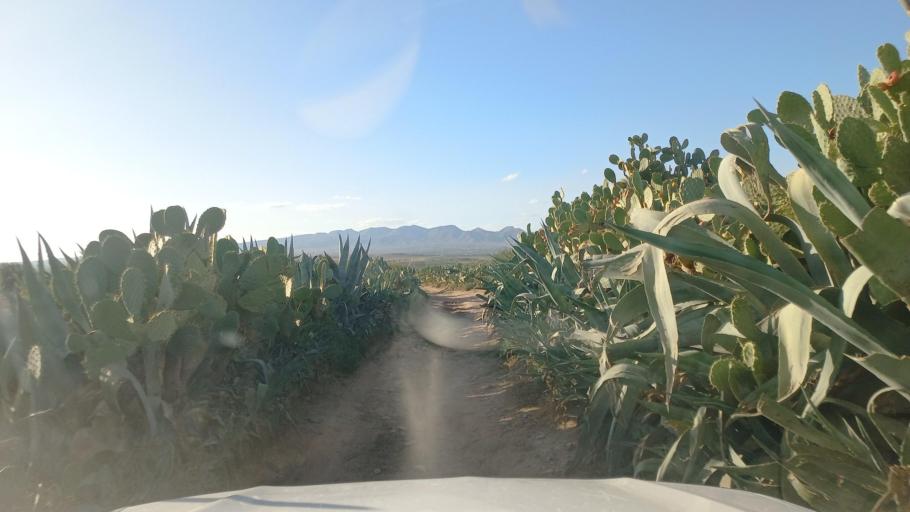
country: TN
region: Al Qasrayn
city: Sbiba
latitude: 35.3850
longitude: 9.1567
